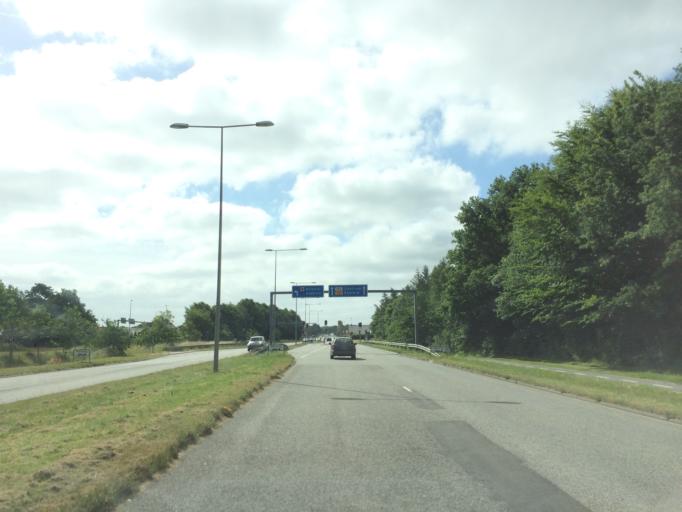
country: DK
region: Central Jutland
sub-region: Herning Kommune
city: Herning
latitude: 56.1437
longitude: 8.9410
